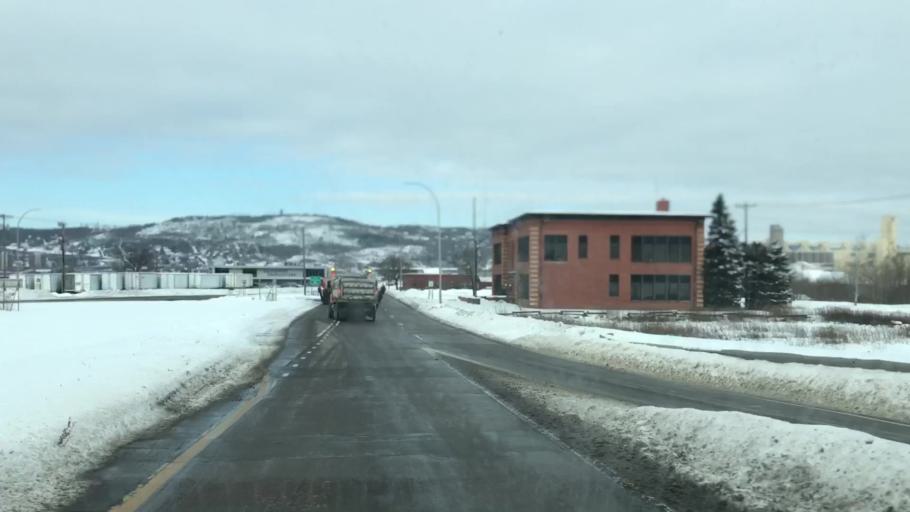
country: US
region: Minnesota
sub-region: Saint Louis County
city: Duluth
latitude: 46.7577
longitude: -92.1076
